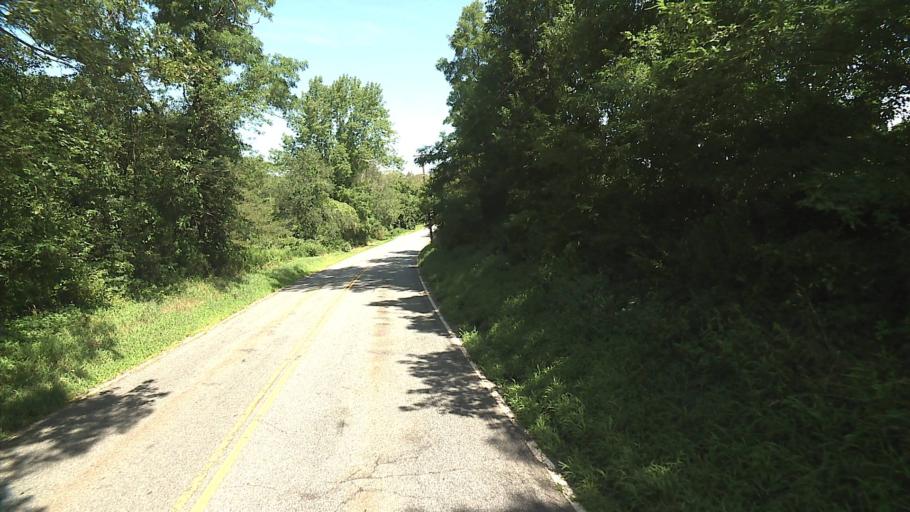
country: US
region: Connecticut
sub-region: Windham County
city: South Woodstock
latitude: 41.8666
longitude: -72.0068
